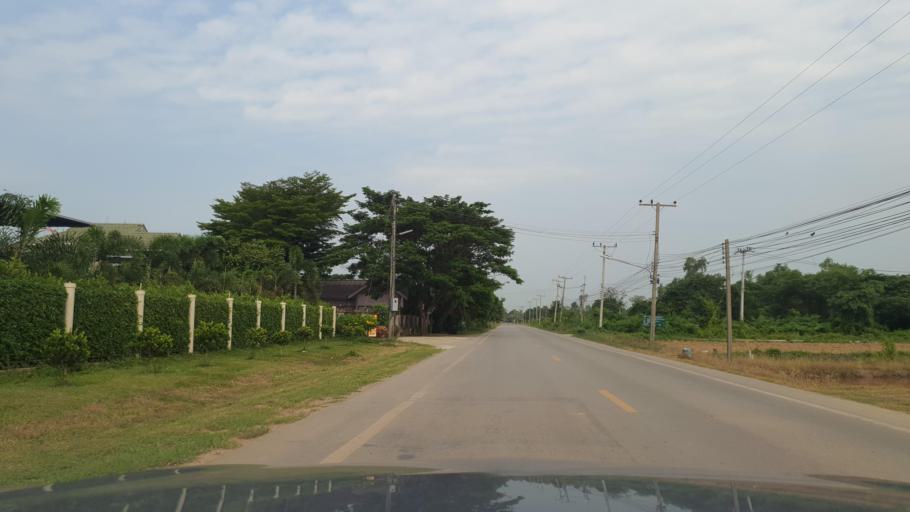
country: TH
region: Phitsanulok
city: Bang Rakam
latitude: 16.8145
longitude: 100.1728
